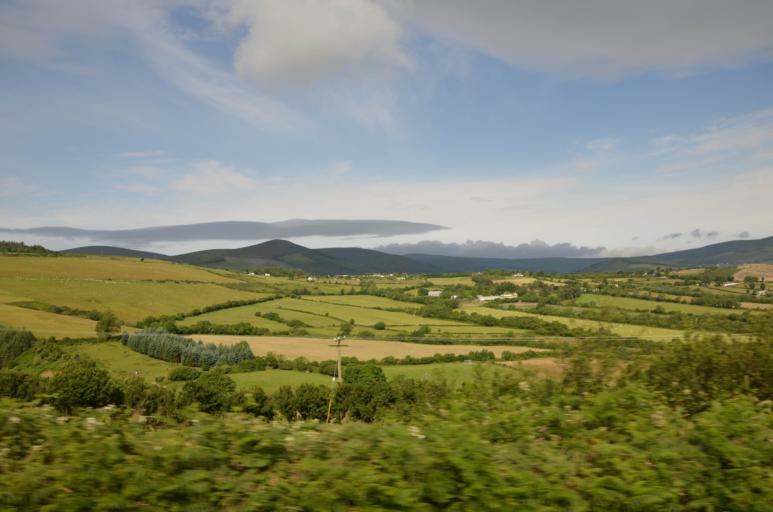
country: IE
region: Leinster
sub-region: Wicklow
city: Kilmacanoge
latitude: 53.1556
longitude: -6.1656
